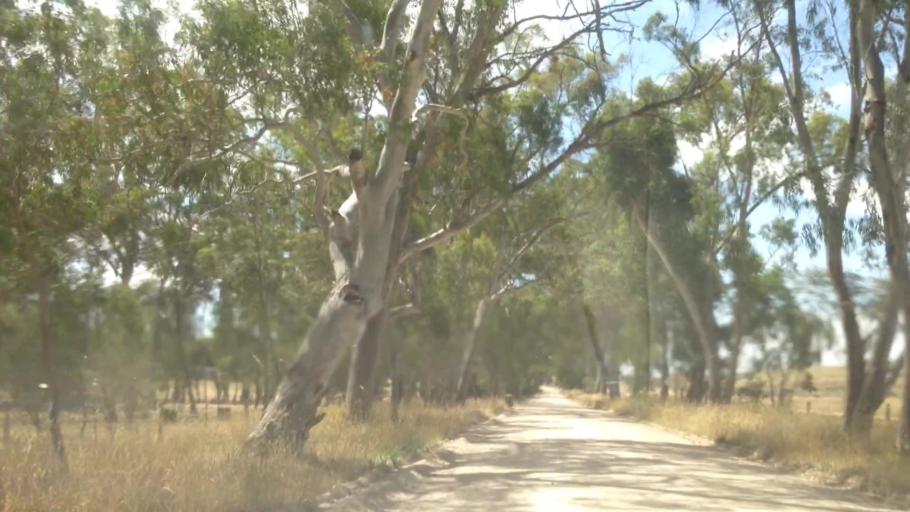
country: AU
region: South Australia
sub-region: Adelaide Hills
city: Birdwood
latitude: -34.7279
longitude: 138.9647
